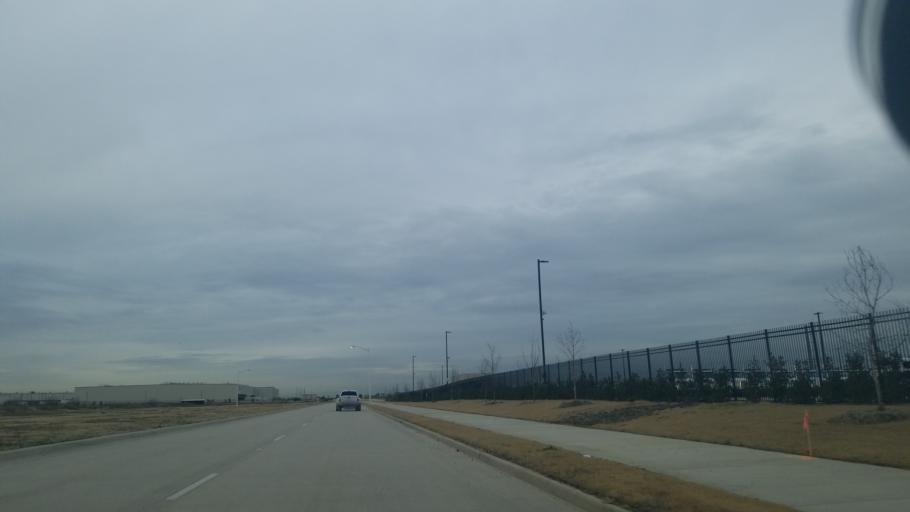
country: US
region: Texas
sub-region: Denton County
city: Denton
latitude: 33.2055
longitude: -97.1849
